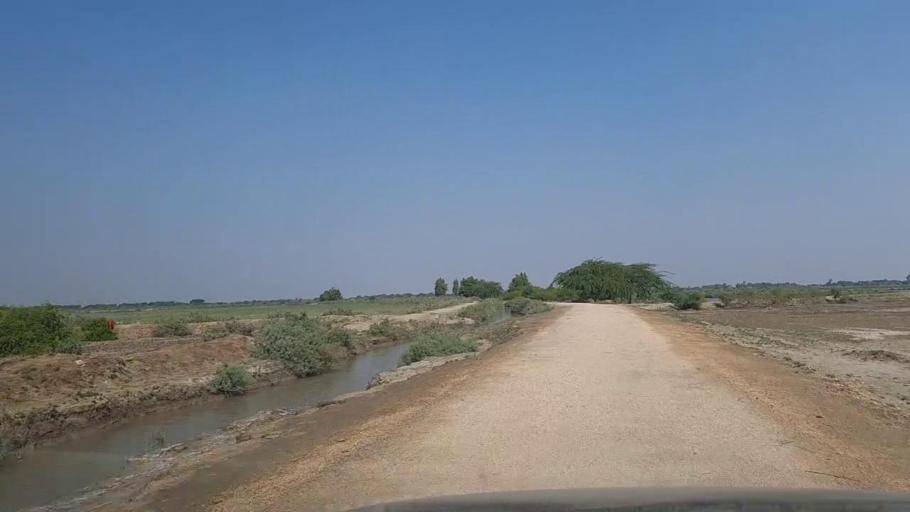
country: PK
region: Sindh
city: Mirpur Sakro
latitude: 24.5081
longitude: 67.7799
